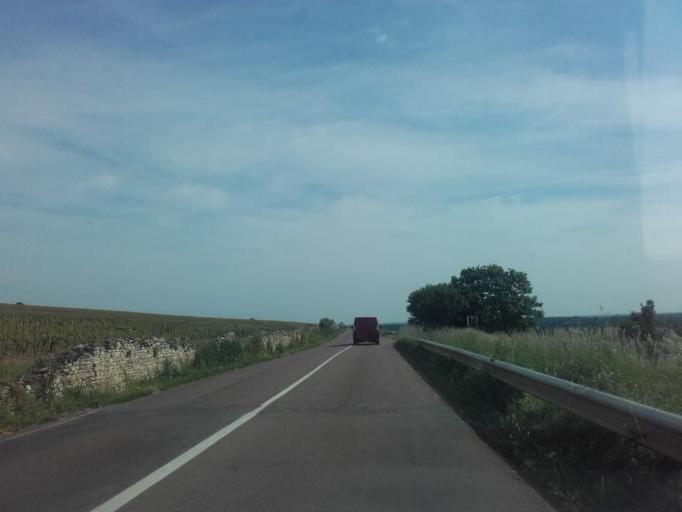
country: FR
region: Bourgogne
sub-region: Departement de Saone-et-Loire
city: Givry
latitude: 46.7918
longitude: 4.7482
